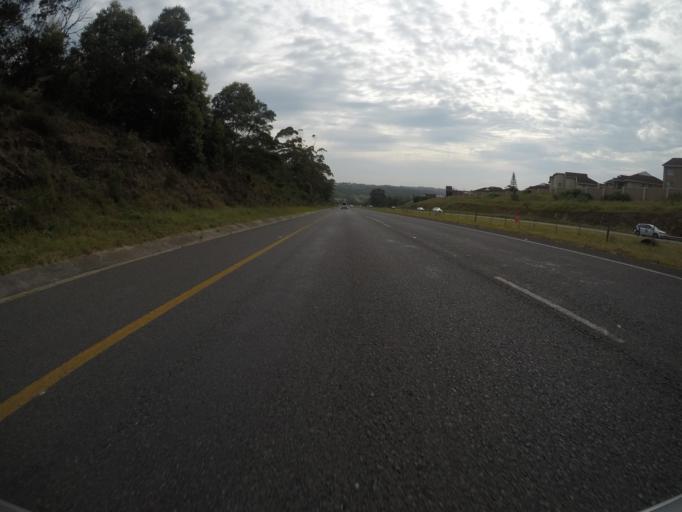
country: ZA
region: Eastern Cape
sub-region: Buffalo City Metropolitan Municipality
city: East London
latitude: -32.9493
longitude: 27.9353
